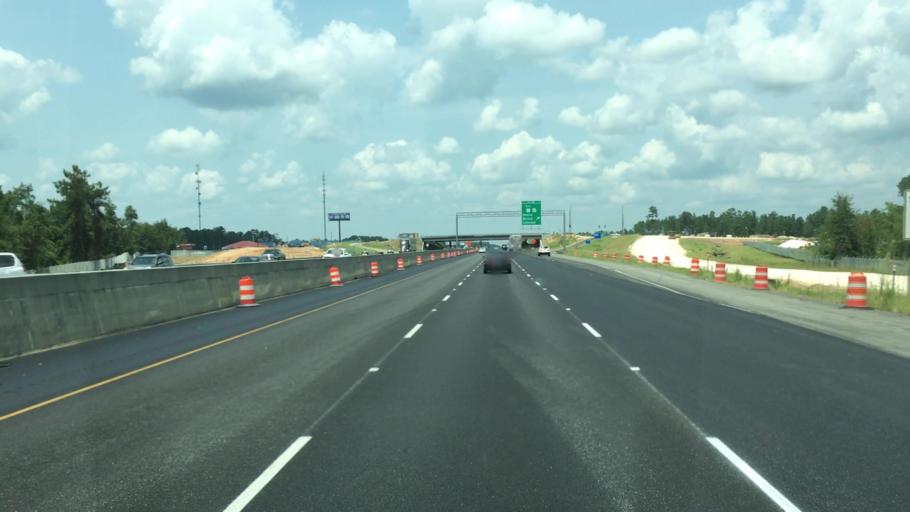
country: US
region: Georgia
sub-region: Lowndes County
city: Hahira
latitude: 30.9879
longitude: -83.3866
